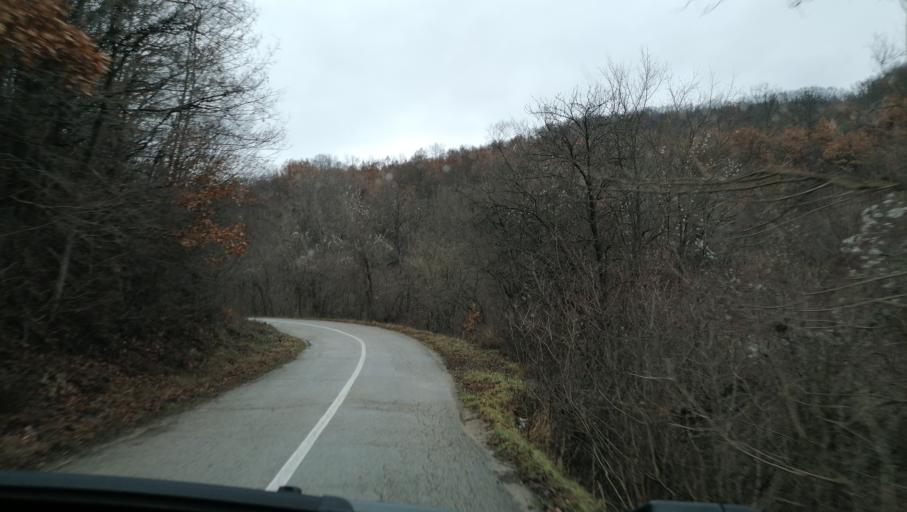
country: RS
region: Central Serbia
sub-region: Pirotski Okrug
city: Dimitrovgrad
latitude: 42.9752
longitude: 22.7852
